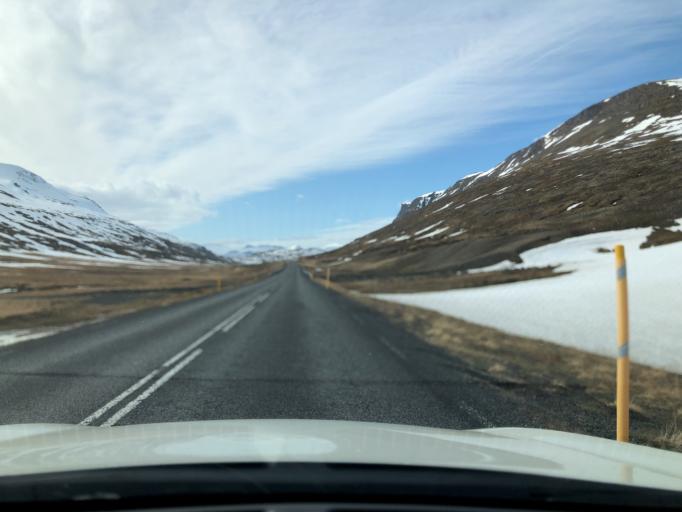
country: IS
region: East
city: Egilsstadir
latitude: 65.1322
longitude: -14.3356
